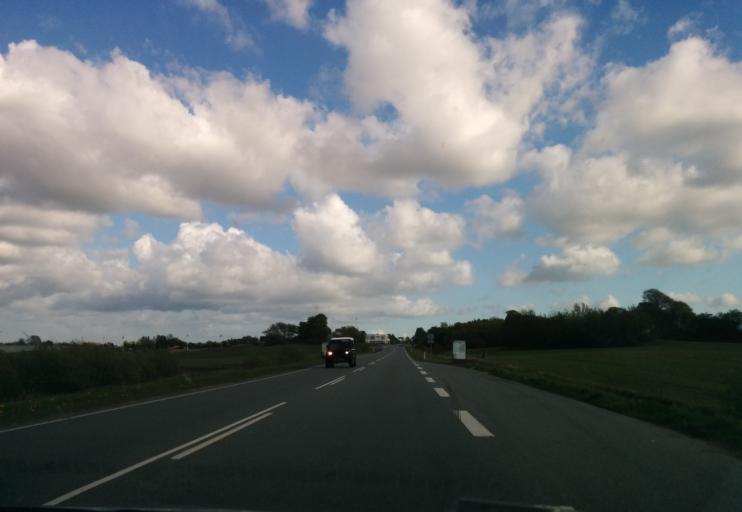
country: DK
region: Central Jutland
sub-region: Arhus Kommune
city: Stavtrup
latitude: 56.1132
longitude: 10.1142
